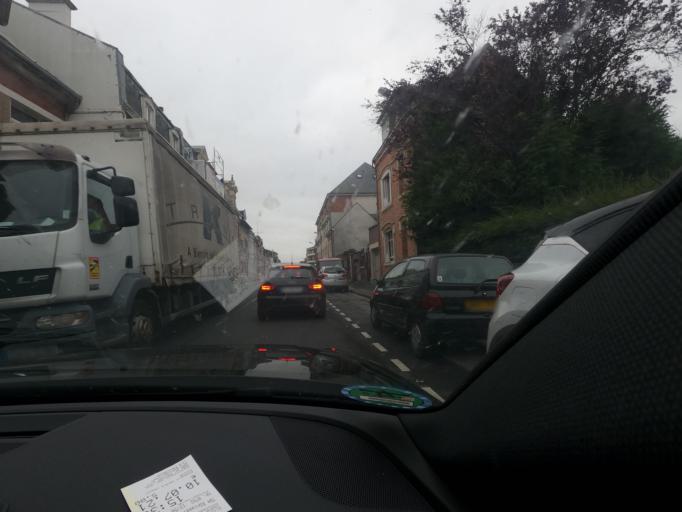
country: FR
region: Picardie
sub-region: Departement de la Somme
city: Amiens
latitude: 49.8798
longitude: 2.3050
